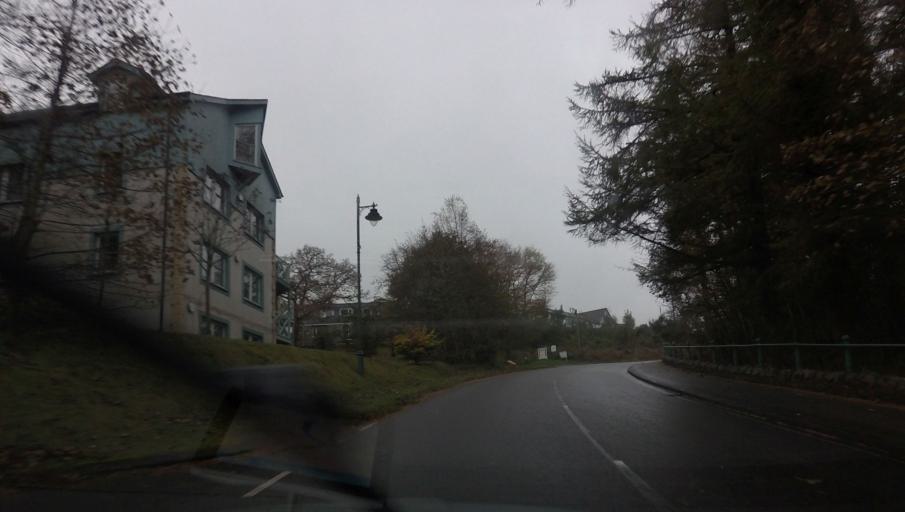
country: GB
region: Scotland
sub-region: Argyll and Bute
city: Isle Of Mull
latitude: 56.6188
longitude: -6.0710
